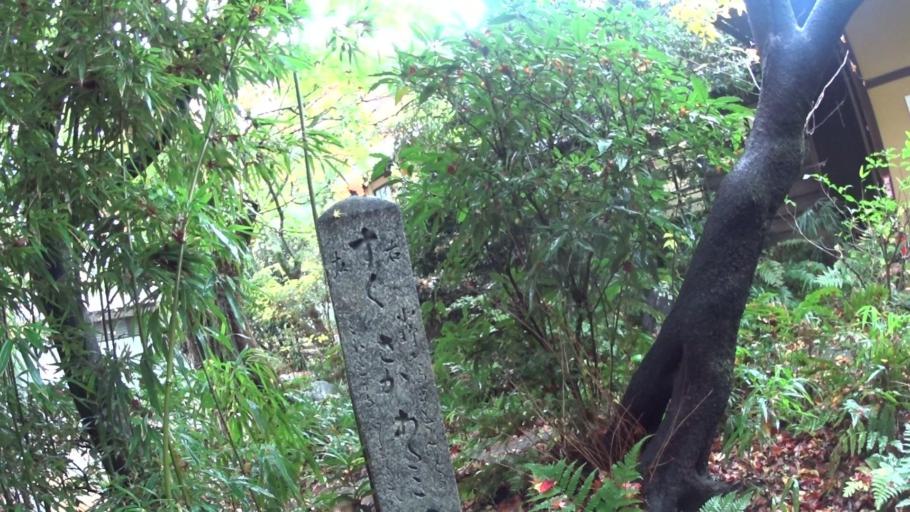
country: JP
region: Kyoto
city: Kyoto
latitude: 35.0307
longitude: 135.7267
